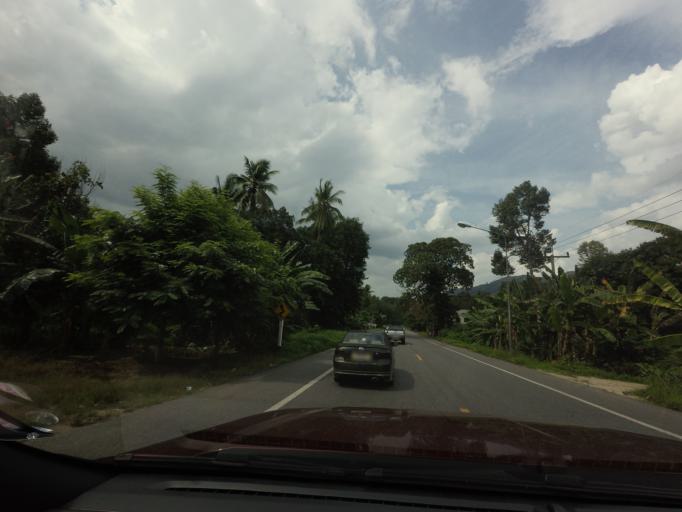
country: TH
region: Yala
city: Ban Nang Sata
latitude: 6.2760
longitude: 101.2867
